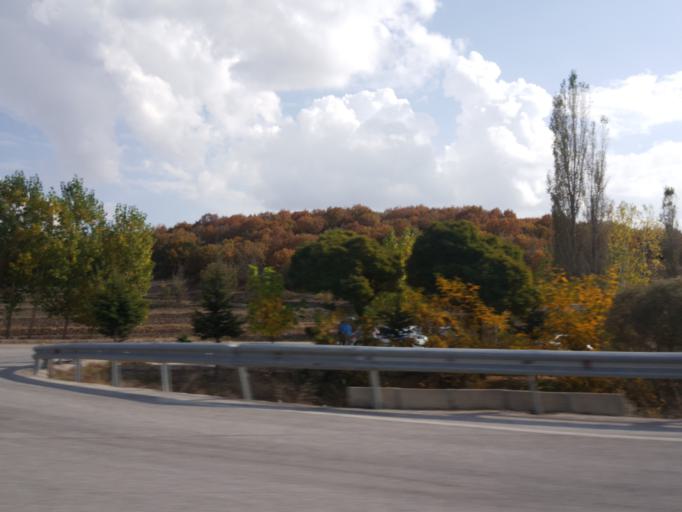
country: TR
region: Corum
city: Alaca
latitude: 40.3230
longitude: 34.6976
